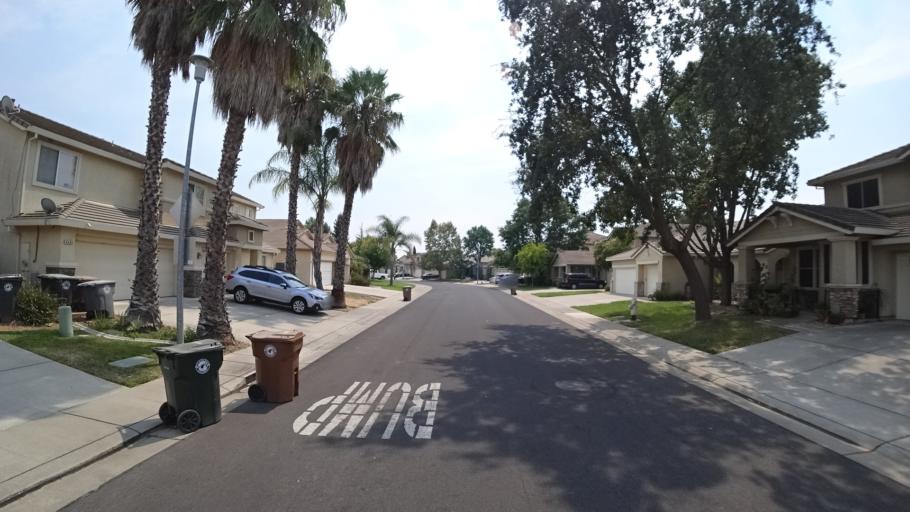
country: US
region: California
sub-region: Sacramento County
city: Laguna
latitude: 38.3877
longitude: -121.4299
